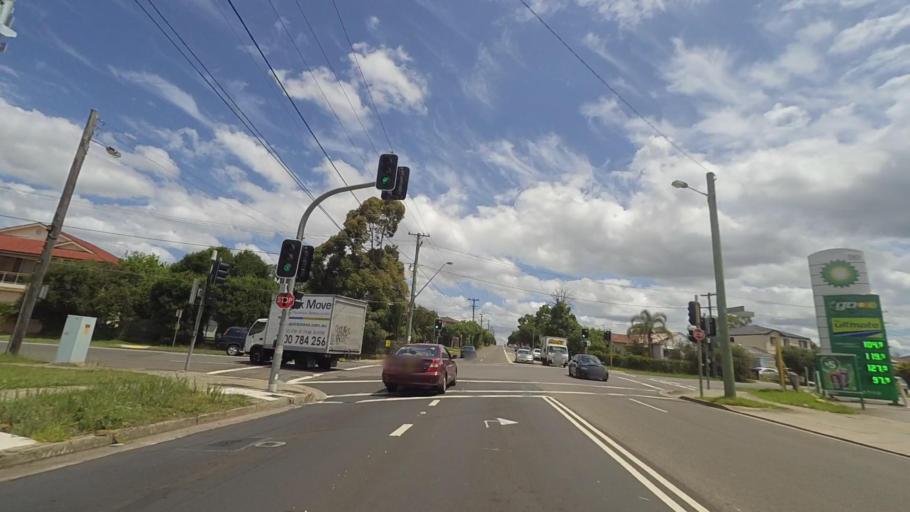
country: AU
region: New South Wales
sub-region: Fairfield
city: Fairfield Heights
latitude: -33.8727
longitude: 150.9457
